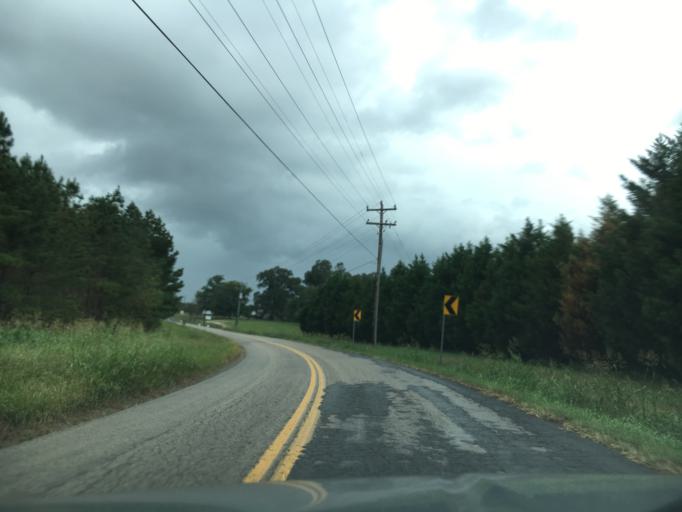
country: US
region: Virginia
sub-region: Amelia County
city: Amelia Court House
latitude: 37.3763
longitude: -77.9766
